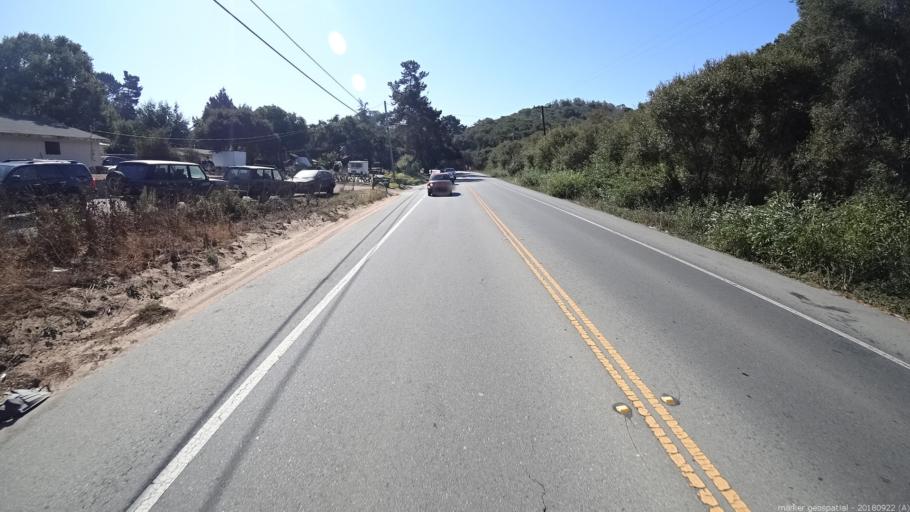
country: US
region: California
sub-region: Monterey County
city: Las Lomas
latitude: 36.8447
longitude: -121.6897
